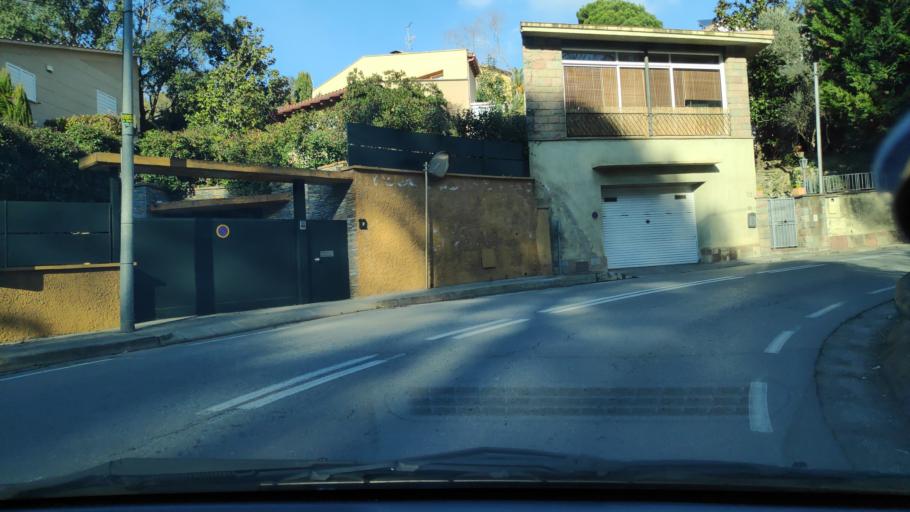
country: ES
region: Catalonia
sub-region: Provincia de Barcelona
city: Sant Quirze del Valles
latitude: 41.5008
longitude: 2.0869
